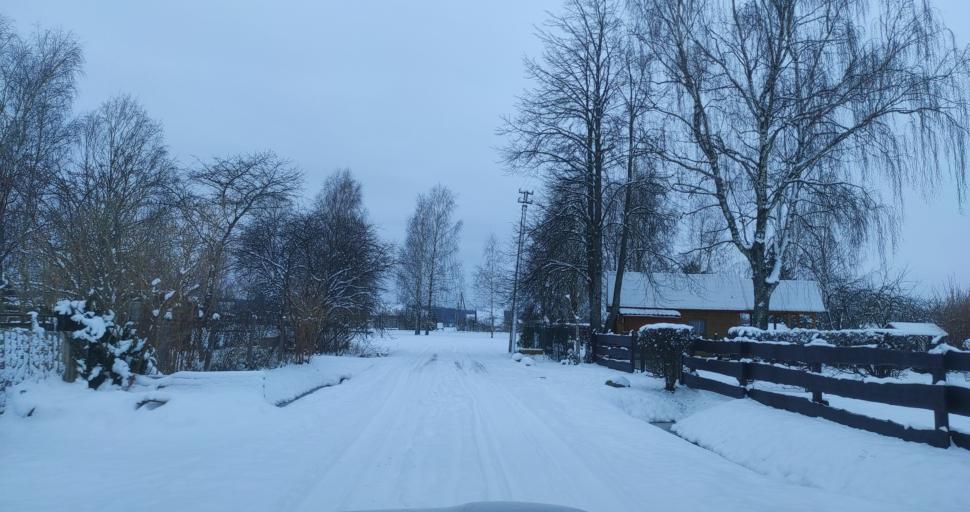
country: LV
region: Kuldigas Rajons
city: Kuldiga
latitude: 56.9513
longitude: 21.9794
